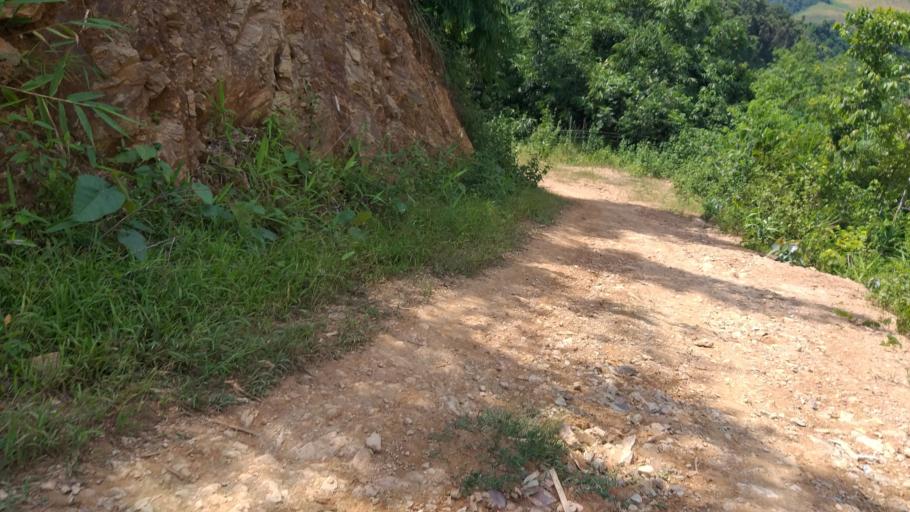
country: LA
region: Phongsali
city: Khoa
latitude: 21.3044
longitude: 102.5622
